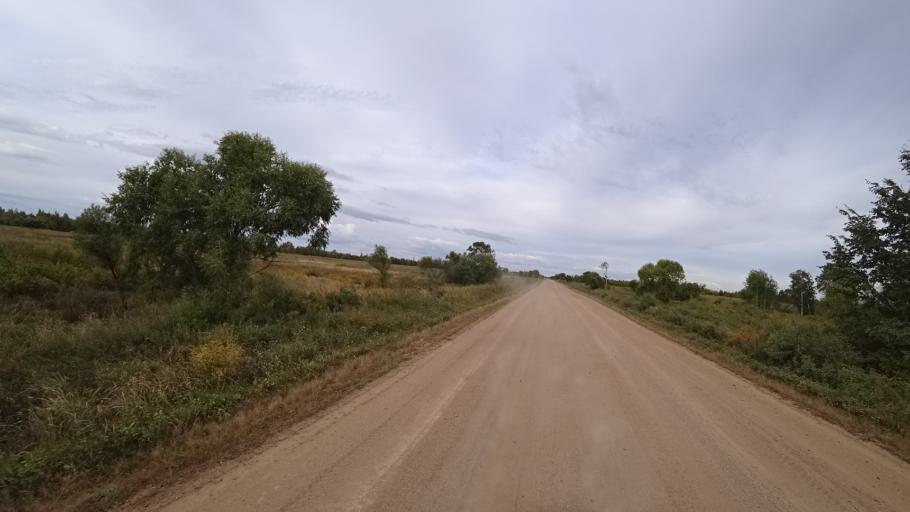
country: RU
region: Amur
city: Arkhara
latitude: 49.3431
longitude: 130.1149
